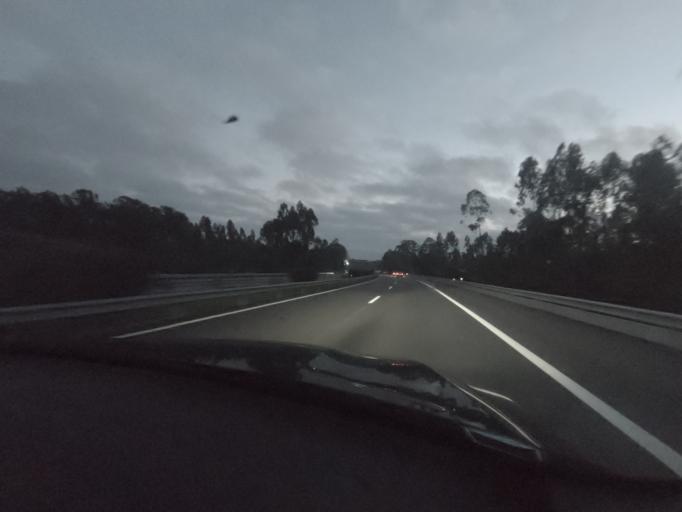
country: PT
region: Leiria
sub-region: Pombal
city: Pombal
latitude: 39.9169
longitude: -8.6846
